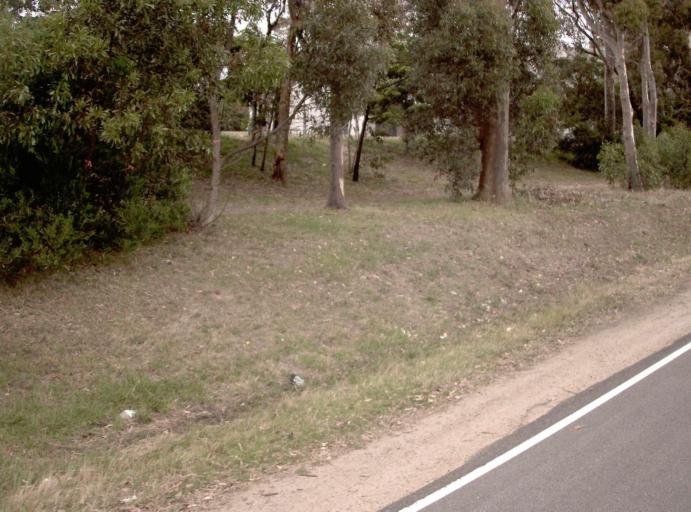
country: AU
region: Victoria
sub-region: Mornington Peninsula
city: Mount Eliza
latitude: -38.1965
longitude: 145.0889
